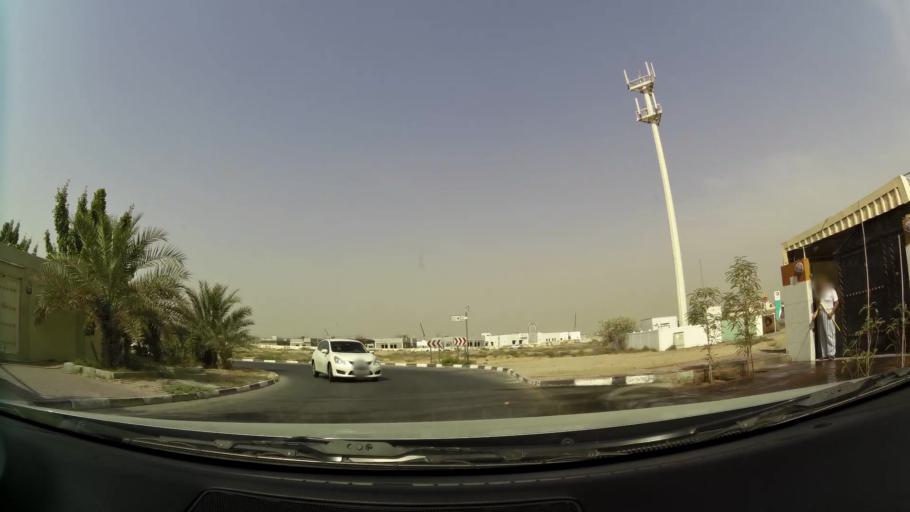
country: AE
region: Ash Shariqah
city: Sharjah
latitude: 25.2589
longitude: 55.4401
